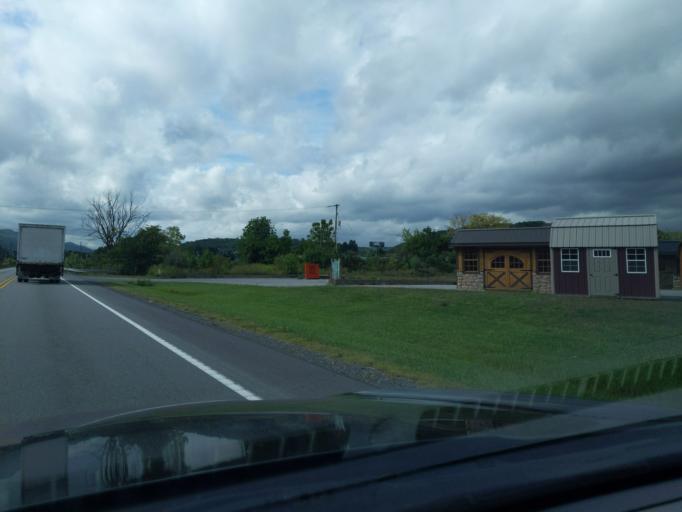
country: US
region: Pennsylvania
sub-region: Blair County
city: Roaring Spring
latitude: 40.3657
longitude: -78.4298
